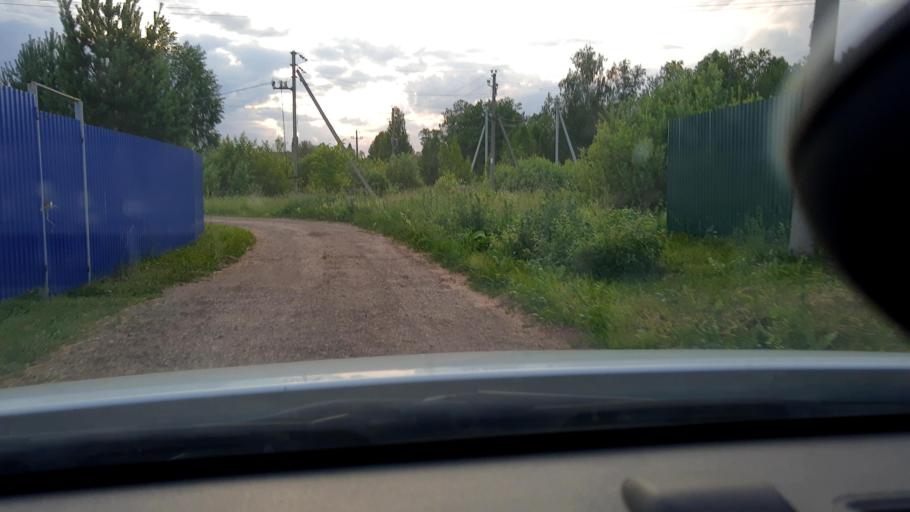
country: RU
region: Bashkortostan
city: Kabakovo
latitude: 54.4416
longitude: 55.9124
